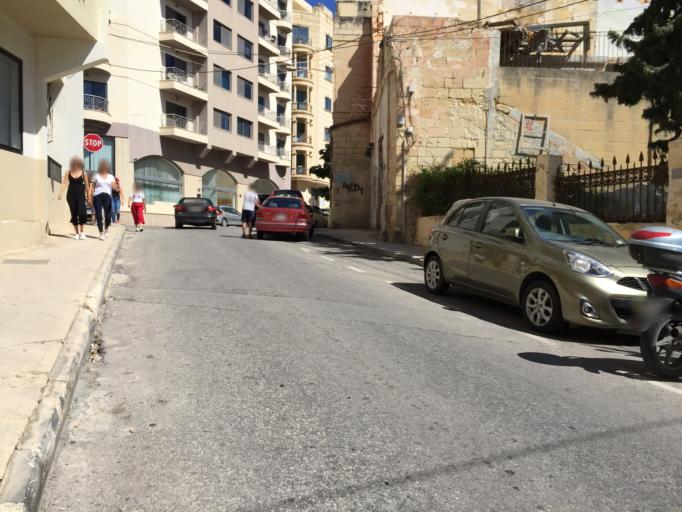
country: MT
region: Tas-Sliema
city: Sliema
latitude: 35.9140
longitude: 14.4954
